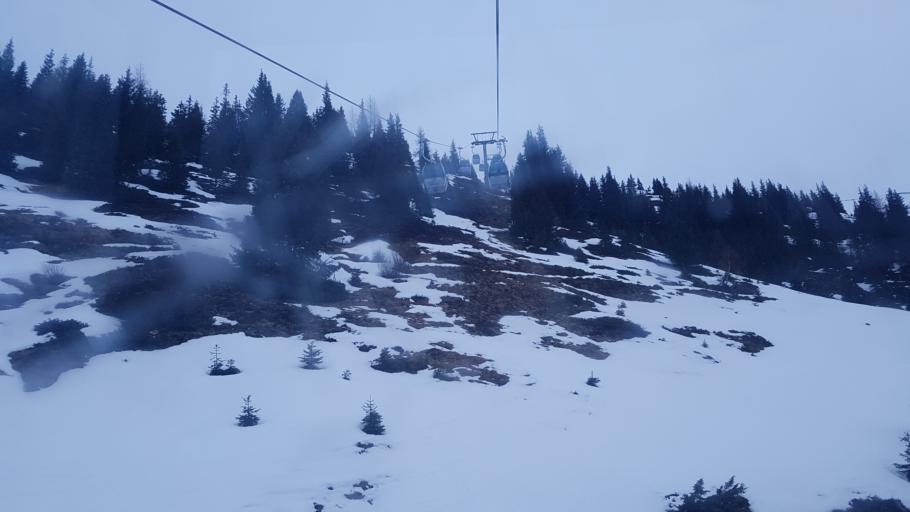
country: AT
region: Salzburg
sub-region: Politischer Bezirk Zell am See
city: Neukirchen am Grossvenediger
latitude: 47.2726
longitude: 12.2812
